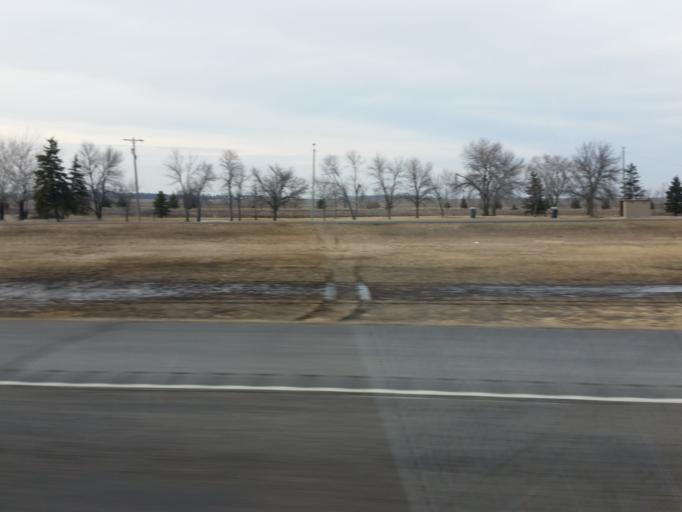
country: US
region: North Dakota
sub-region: Cass County
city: Casselton
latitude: 46.8770
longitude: -97.0882
